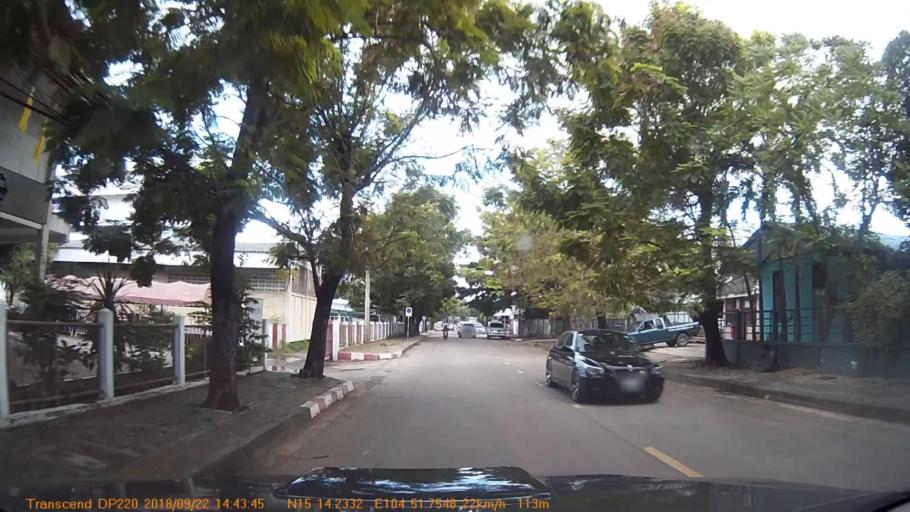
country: TH
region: Changwat Ubon Ratchathani
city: Ubon Ratchathani
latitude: 15.2370
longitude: 104.8626
